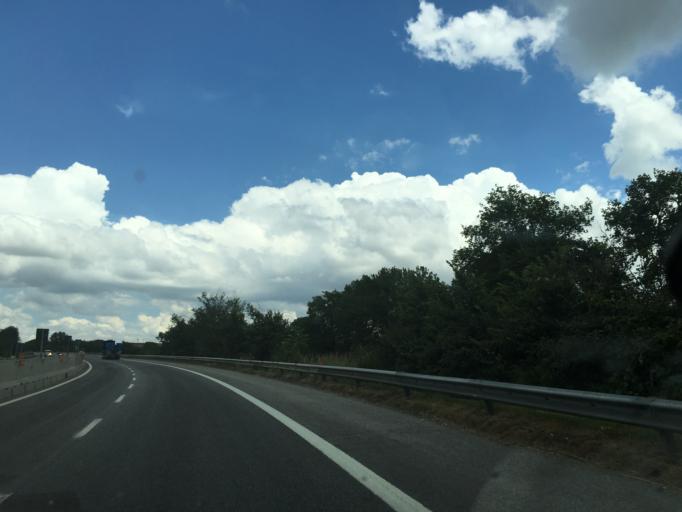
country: IT
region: Campania
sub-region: Provincia di Avellino
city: Passo di Mirabella-Pianopantano
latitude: 41.0582
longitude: 15.0311
